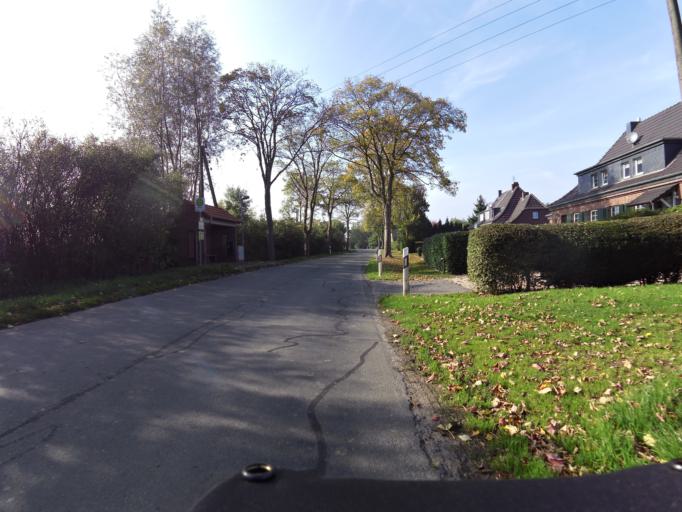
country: DE
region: North Rhine-Westphalia
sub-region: Regierungsbezirk Dusseldorf
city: Kranenburg
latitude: 51.8254
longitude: 6.0138
